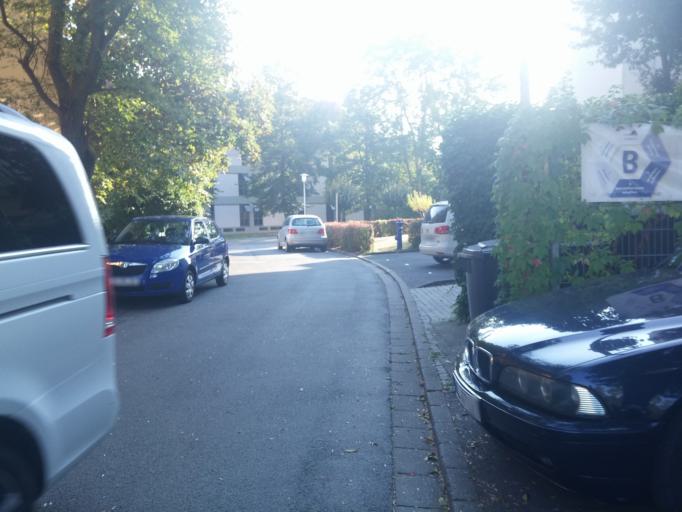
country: DE
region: Bavaria
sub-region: Upper Franconia
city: Coburg
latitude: 50.2571
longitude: 10.9611
